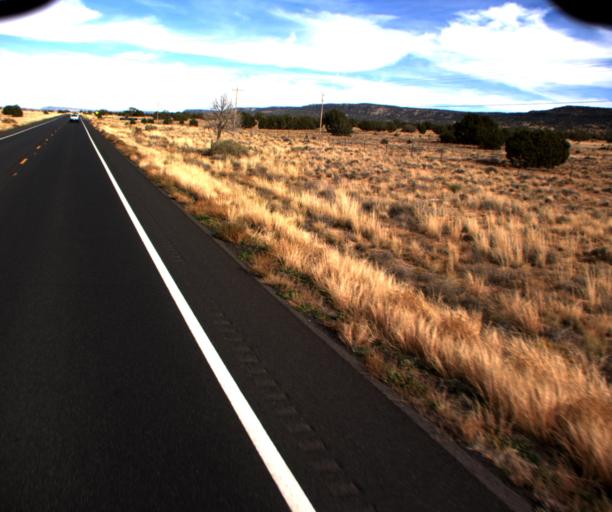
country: US
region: Arizona
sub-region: Coconino County
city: Kaibito
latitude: 36.4826
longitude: -110.6454
